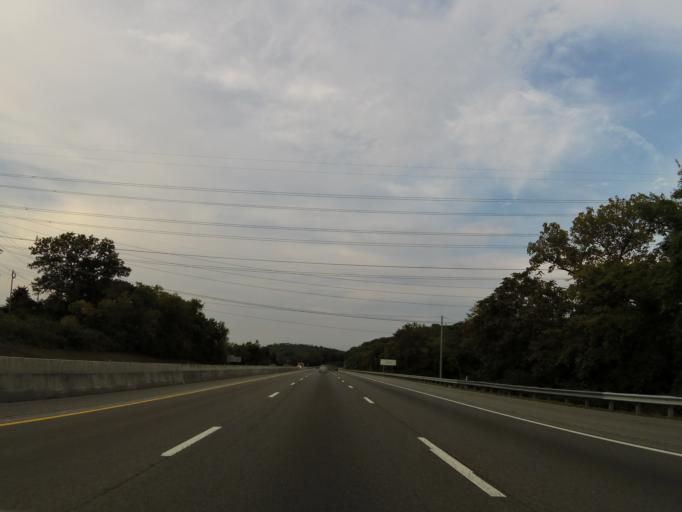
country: US
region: Tennessee
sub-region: Davidson County
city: Belle Meade
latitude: 36.1198
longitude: -86.9121
